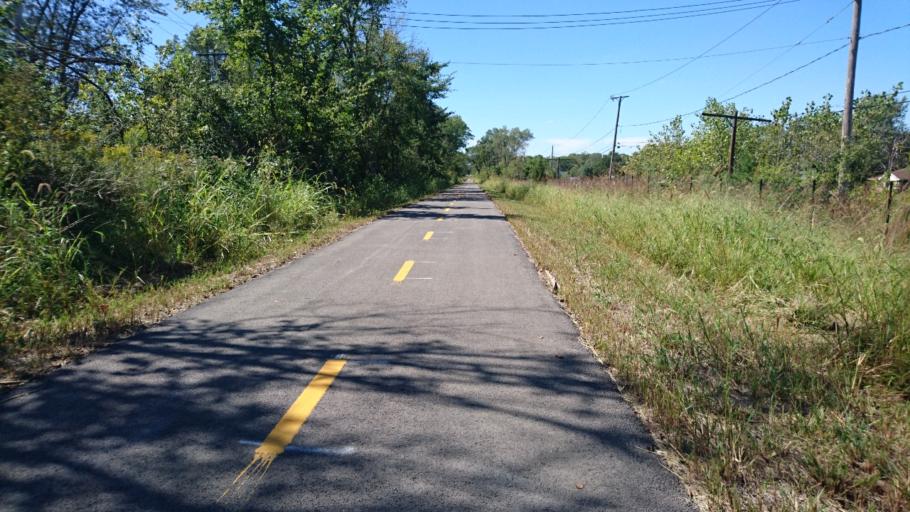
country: US
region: Illinois
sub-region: Cook County
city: Park Forest
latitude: 41.4991
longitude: -87.6649
